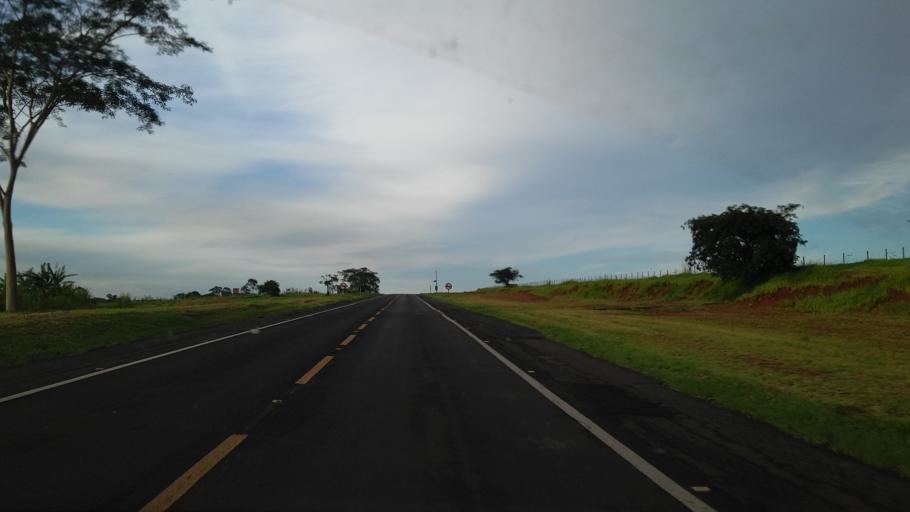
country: BR
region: Sao Paulo
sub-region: Lins
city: Lins
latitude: -21.9162
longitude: -49.9156
